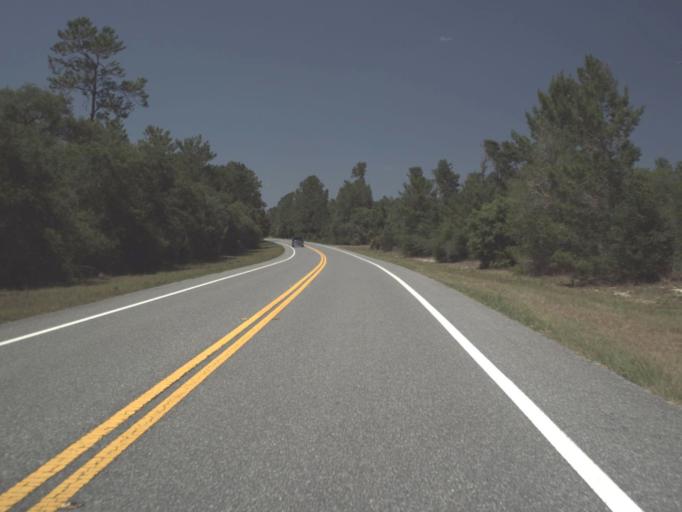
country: US
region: Florida
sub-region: Lake County
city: Astor
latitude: 29.1233
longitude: -81.6189
